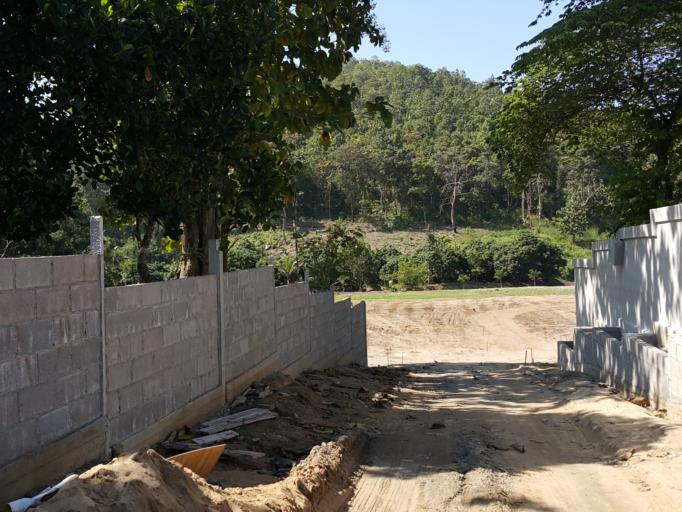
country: TH
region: Chiang Mai
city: Mae On
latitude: 18.7129
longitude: 99.2010
